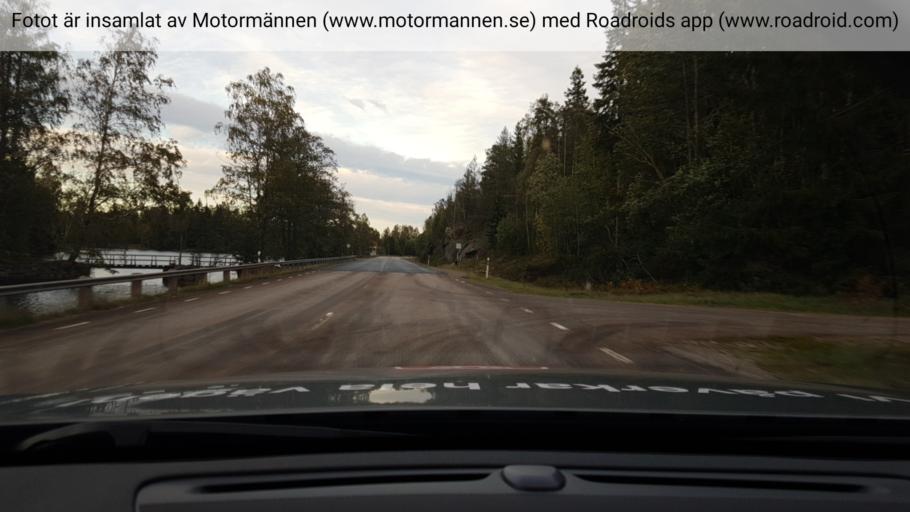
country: SE
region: Vaestra Goetaland
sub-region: Amals Kommun
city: Amal
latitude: 59.0777
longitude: 12.6014
